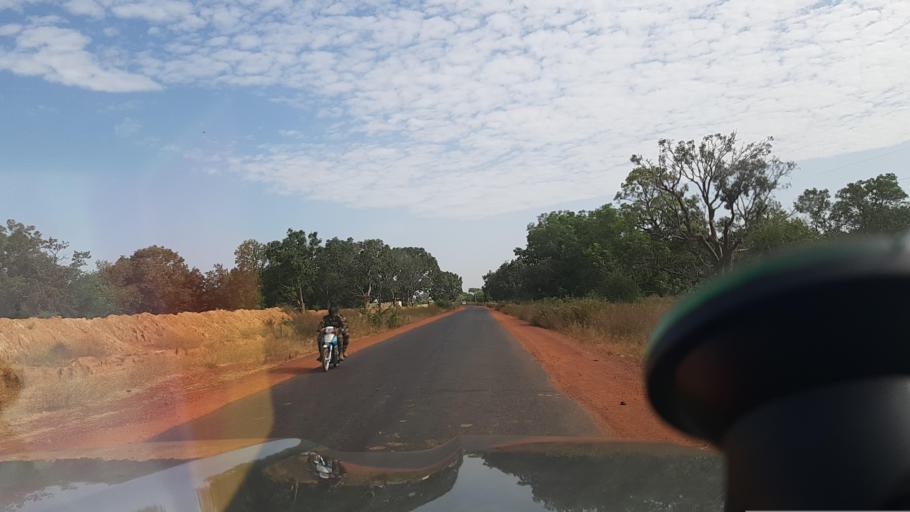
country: ML
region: Segou
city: Segou
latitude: 13.5276
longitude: -6.1294
